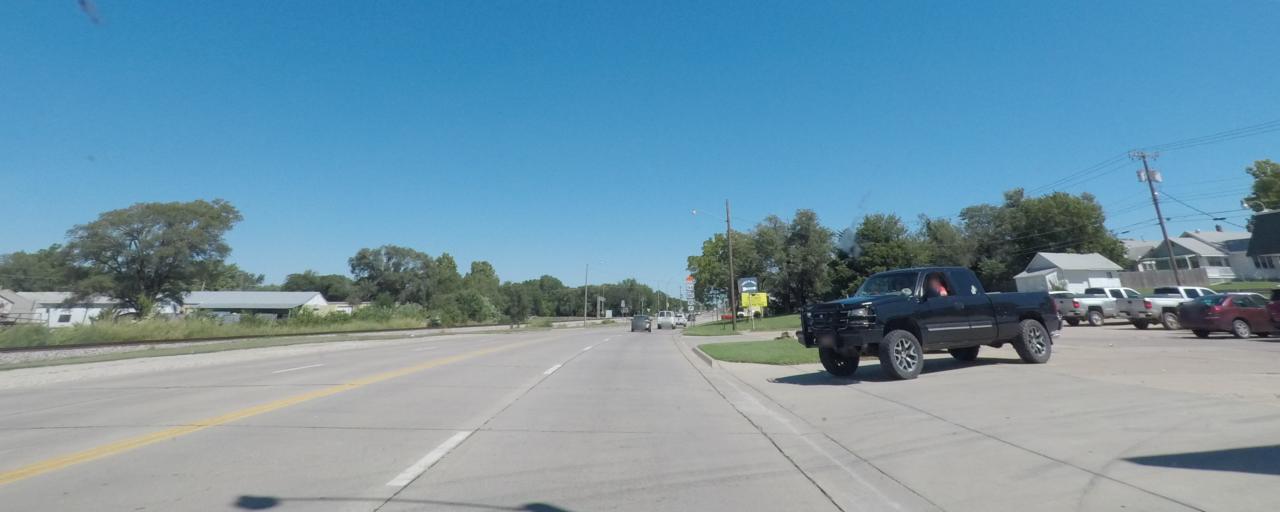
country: US
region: Kansas
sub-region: Sumner County
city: Wellington
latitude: 37.2721
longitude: -97.4020
